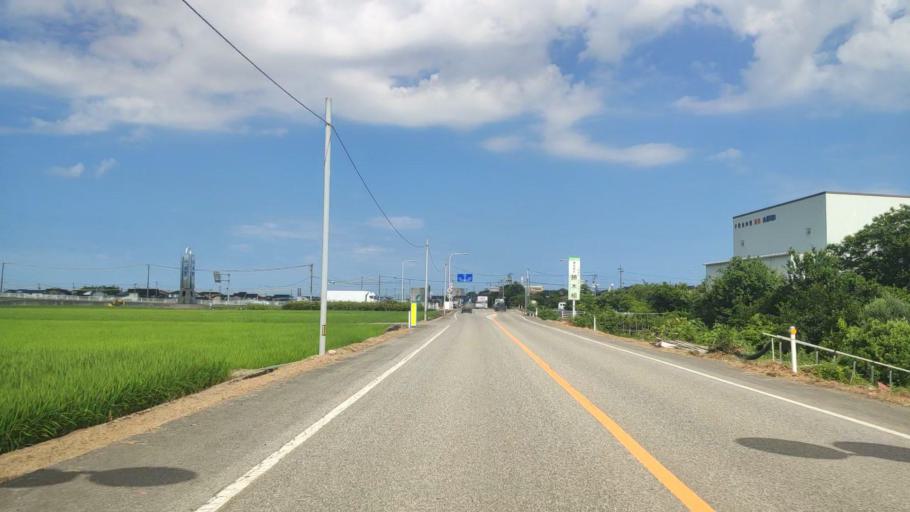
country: JP
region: Ishikawa
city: Matsuto
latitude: 36.4680
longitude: 136.5816
